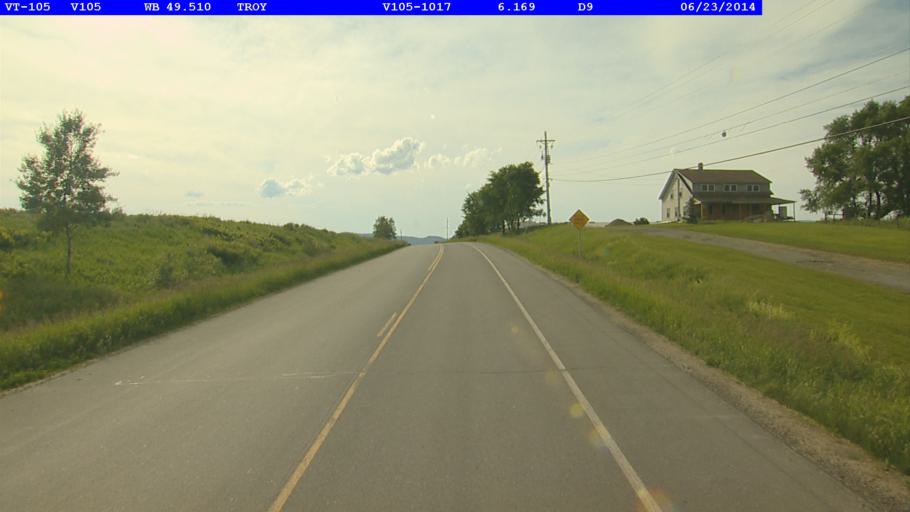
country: US
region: Vermont
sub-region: Orleans County
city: Newport
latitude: 44.9786
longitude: -72.3390
